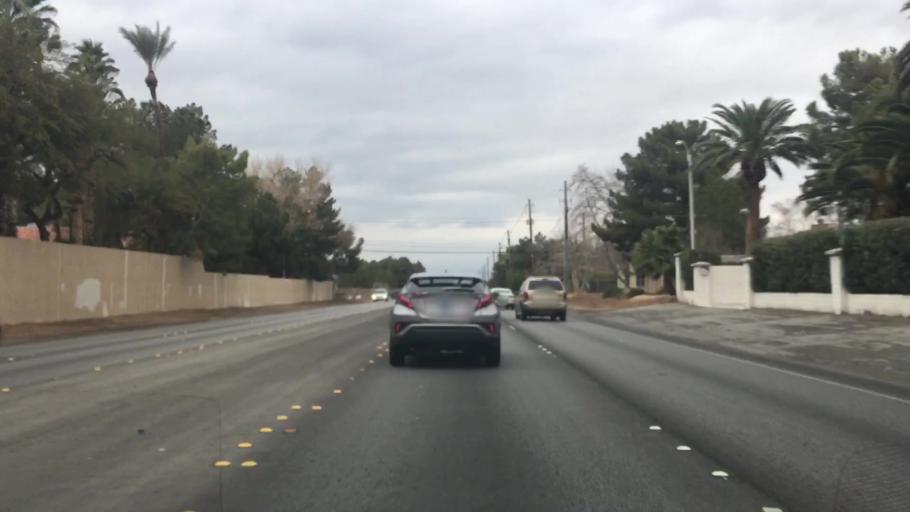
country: US
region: Nevada
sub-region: Clark County
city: Whitney
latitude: 36.0630
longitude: -115.1005
